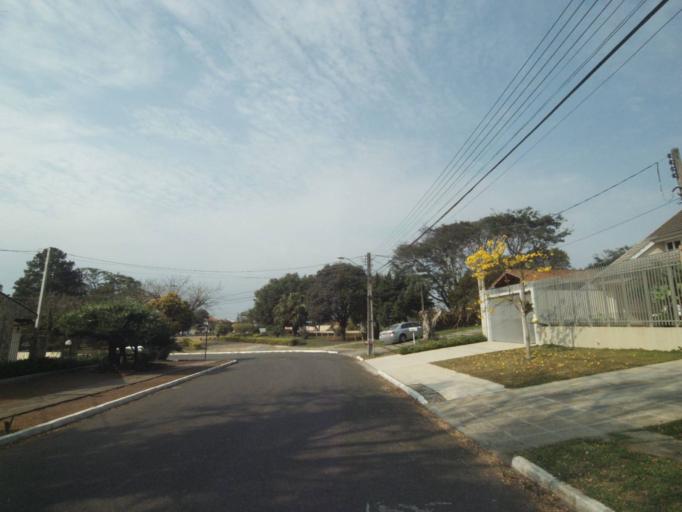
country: BR
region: Parana
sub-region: Pinhais
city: Pinhais
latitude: -25.4822
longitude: -49.2069
